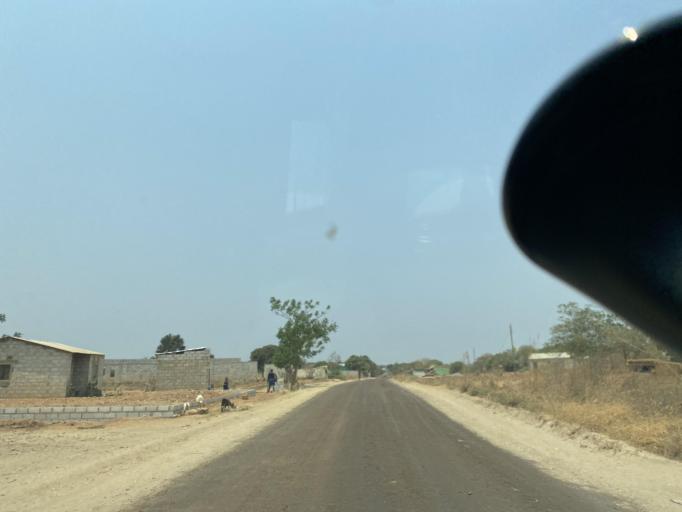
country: ZM
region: Lusaka
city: Lusaka
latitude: -15.5480
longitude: 28.3600
